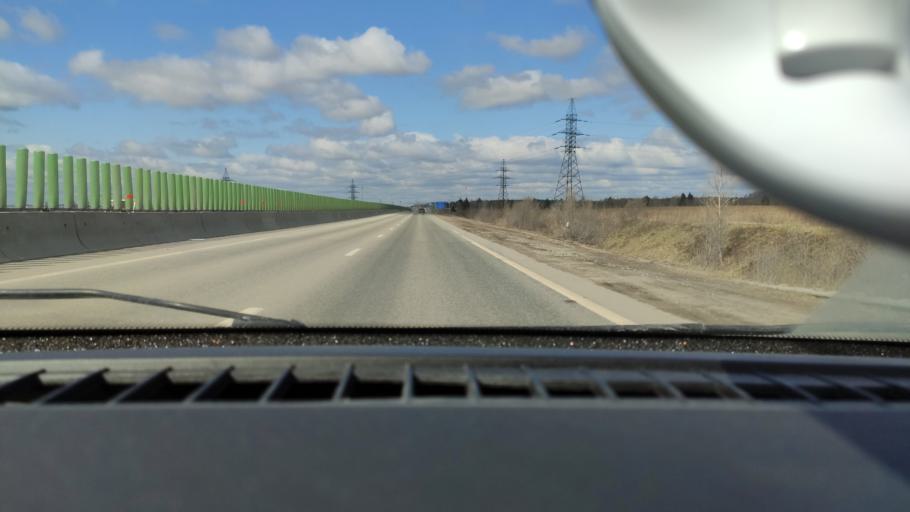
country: RU
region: Perm
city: Froly
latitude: 57.9323
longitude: 56.2853
